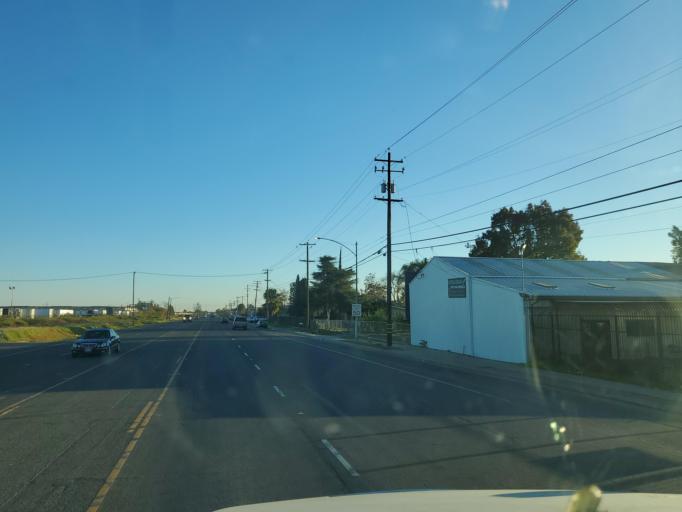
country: US
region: California
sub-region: San Joaquin County
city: Taft Mosswood
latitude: 37.9230
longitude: -121.2804
